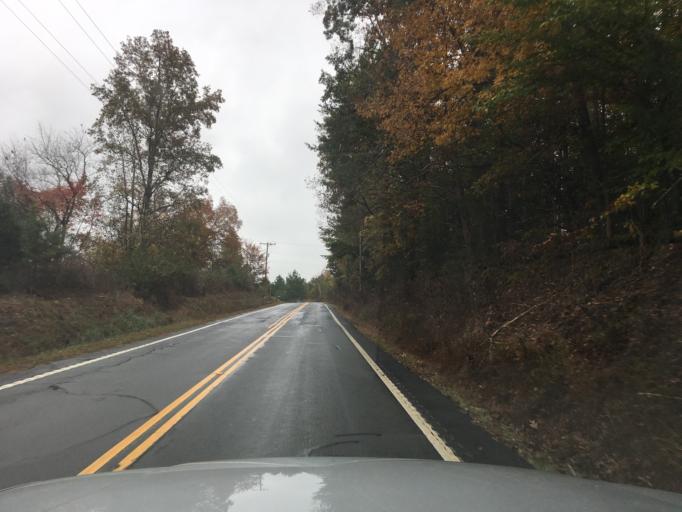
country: US
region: South Carolina
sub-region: Pickens County
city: Liberty
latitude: 34.7549
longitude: -82.7257
